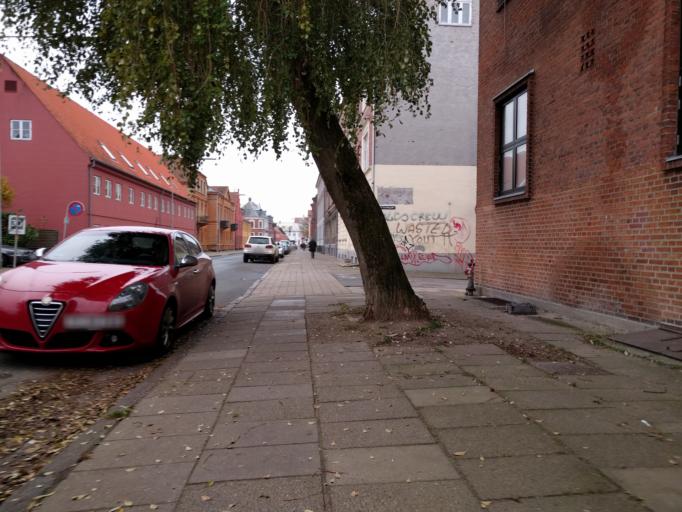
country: DK
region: Capital Region
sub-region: Helsingor Kommune
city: Helsingor
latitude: 56.0391
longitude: 12.6078
